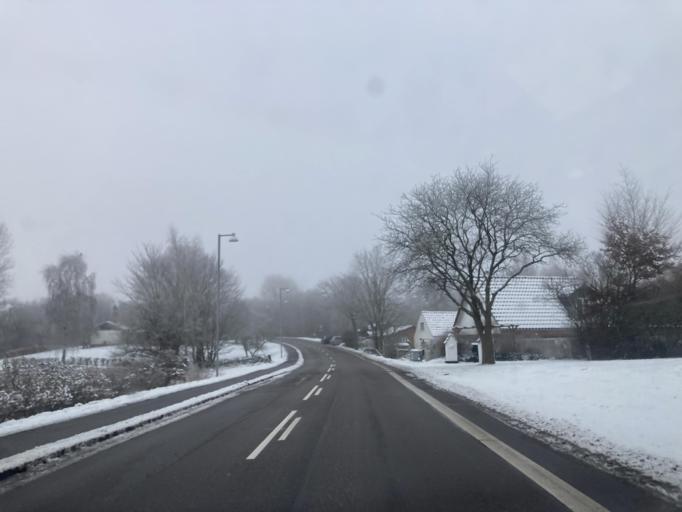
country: DK
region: Zealand
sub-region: Soro Kommune
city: Stenlille
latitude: 55.5436
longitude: 11.6012
